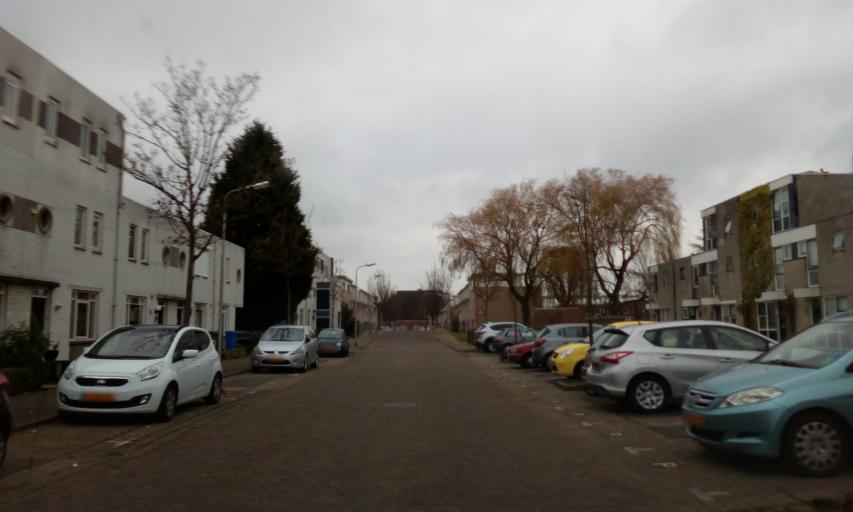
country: NL
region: South Holland
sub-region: Gemeente Delft
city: Delft
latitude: 51.9809
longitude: 4.3384
